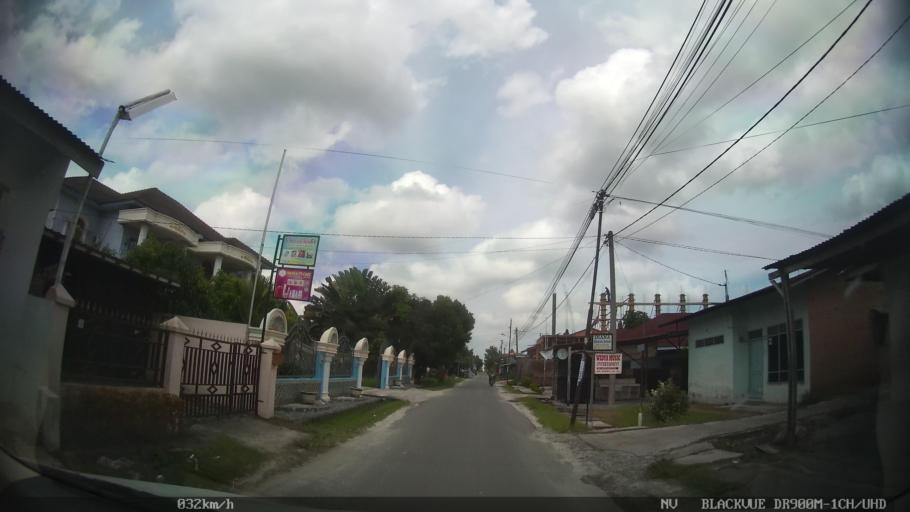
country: ID
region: North Sumatra
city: Percut
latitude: 3.5704
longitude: 98.8651
